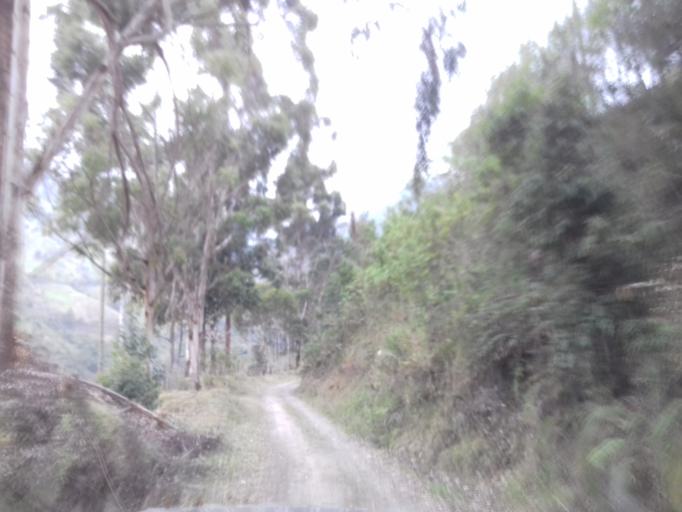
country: CO
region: Tolima
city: Cajamarca
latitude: 4.5341
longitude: -75.4684
